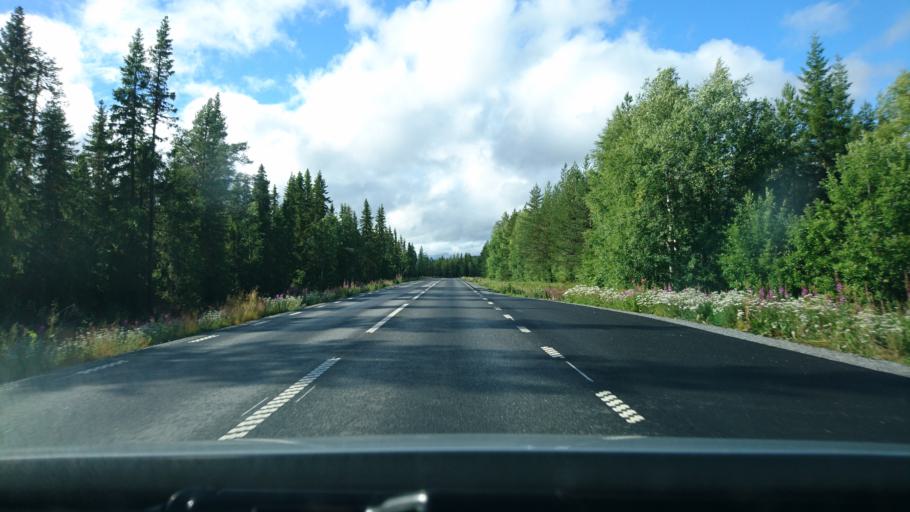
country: SE
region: Vaesterbotten
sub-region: Vilhelmina Kommun
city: Vilhelmina
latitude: 64.6974
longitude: 16.7135
